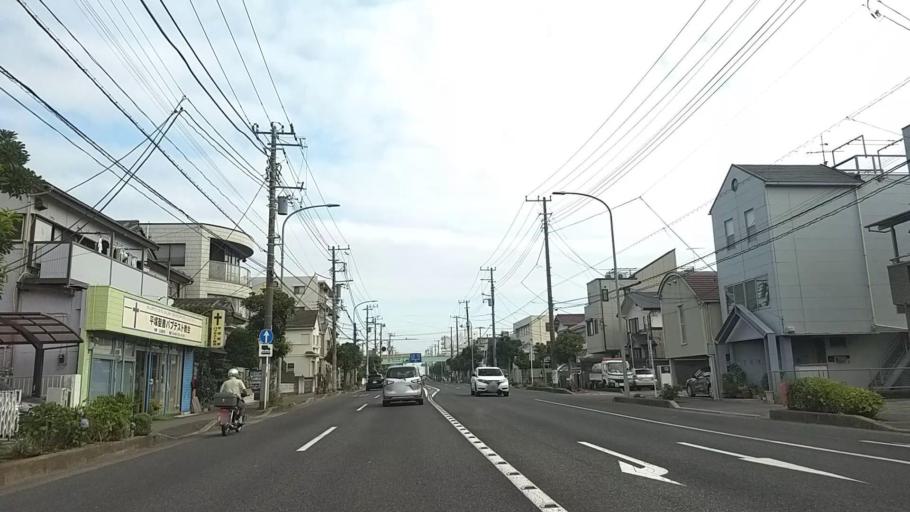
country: JP
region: Kanagawa
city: Hiratsuka
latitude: 35.3208
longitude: 139.3613
